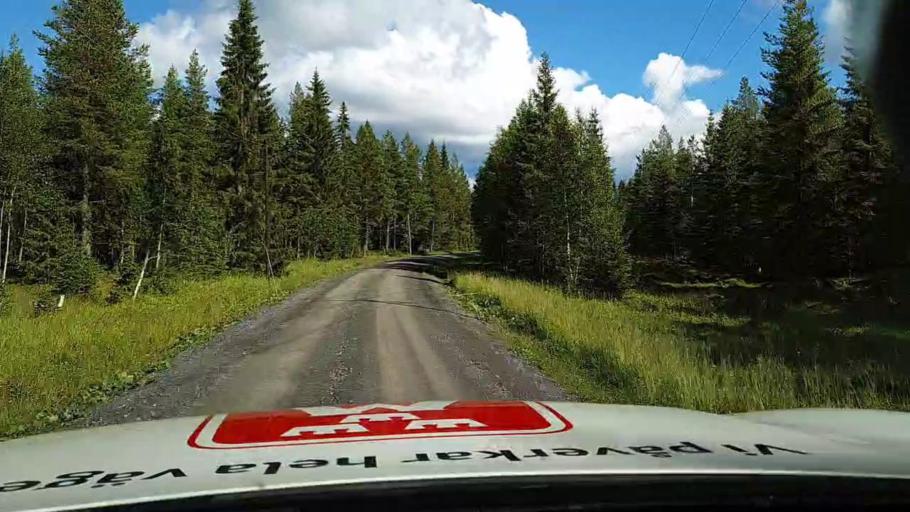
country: SE
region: Jaemtland
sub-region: Krokoms Kommun
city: Valla
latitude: 63.3336
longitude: 13.7201
